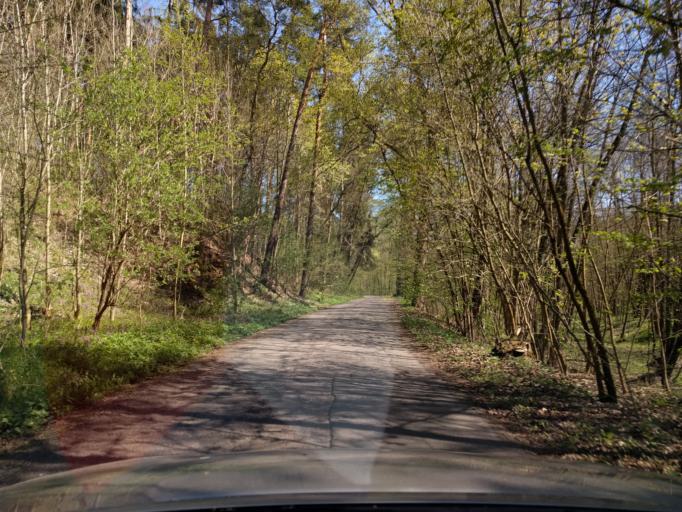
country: CZ
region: Central Bohemia
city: Cesky Brod
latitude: 50.0405
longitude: 14.8378
